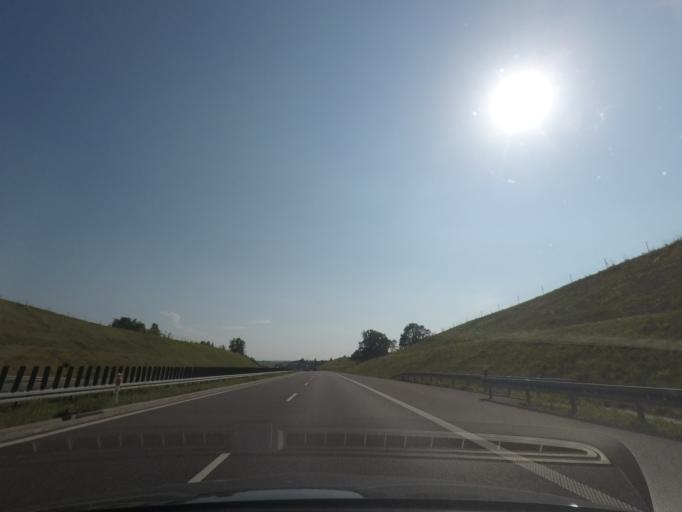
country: PL
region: Silesian Voivodeship
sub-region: Powiat rybnicki
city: Swierklany Dolne
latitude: 50.0114
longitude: 18.5861
